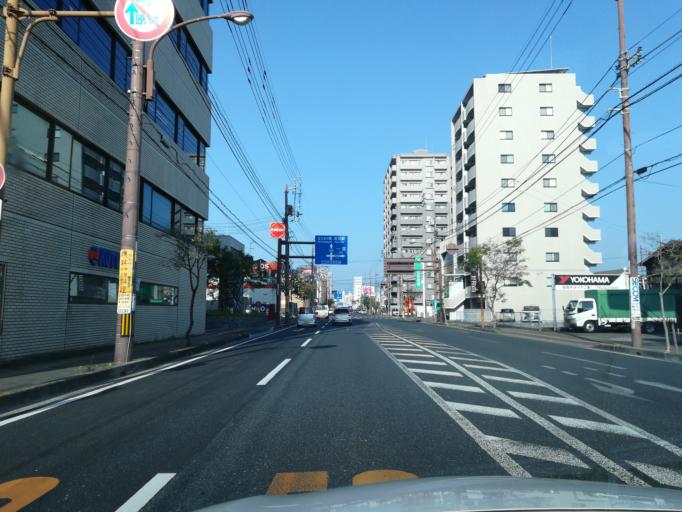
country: JP
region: Kochi
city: Kochi-shi
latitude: 33.5658
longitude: 133.5504
